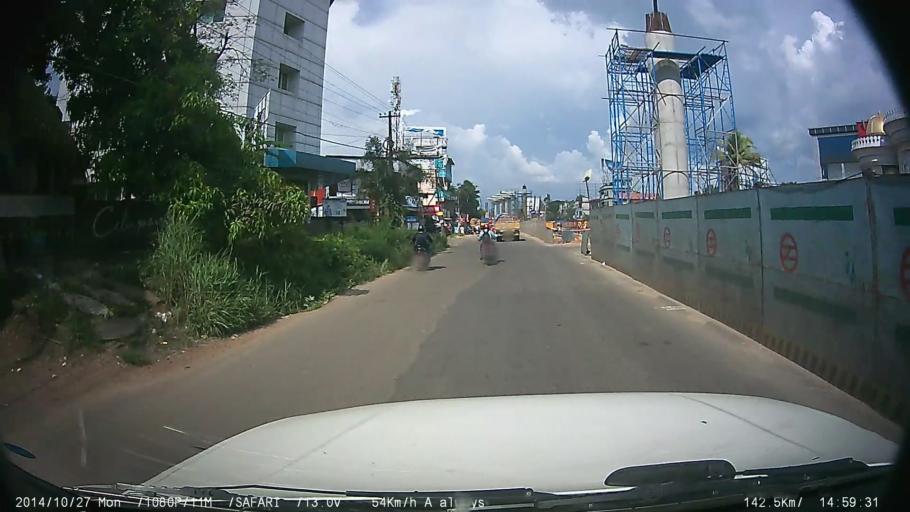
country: IN
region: Kerala
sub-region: Ernakulam
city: Aluva
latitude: 10.0701
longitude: 76.3311
